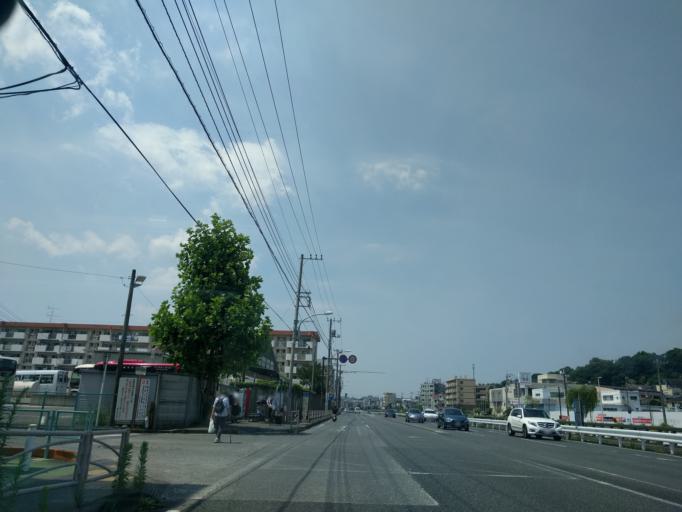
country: JP
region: Kanagawa
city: Yokohama
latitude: 35.4195
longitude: 139.6257
